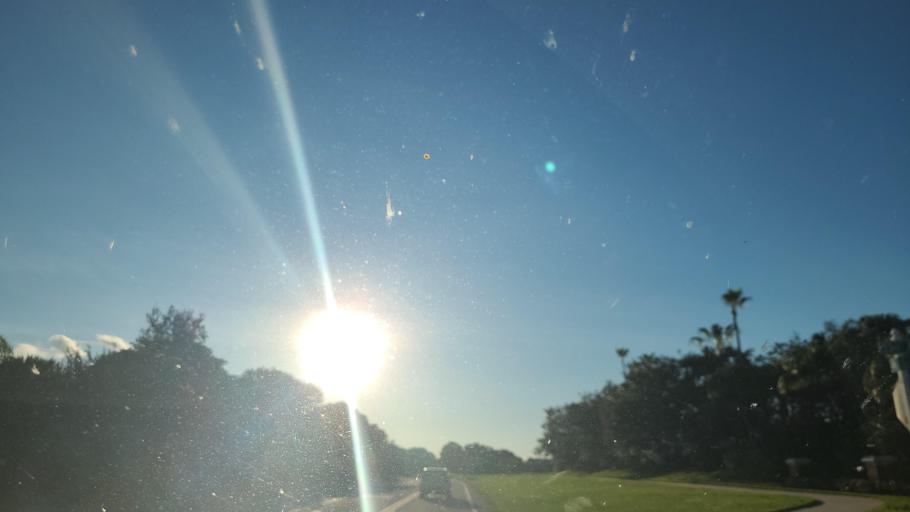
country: US
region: Florida
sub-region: Indian River County
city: Vero Beach South
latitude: 27.6093
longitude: -80.4410
